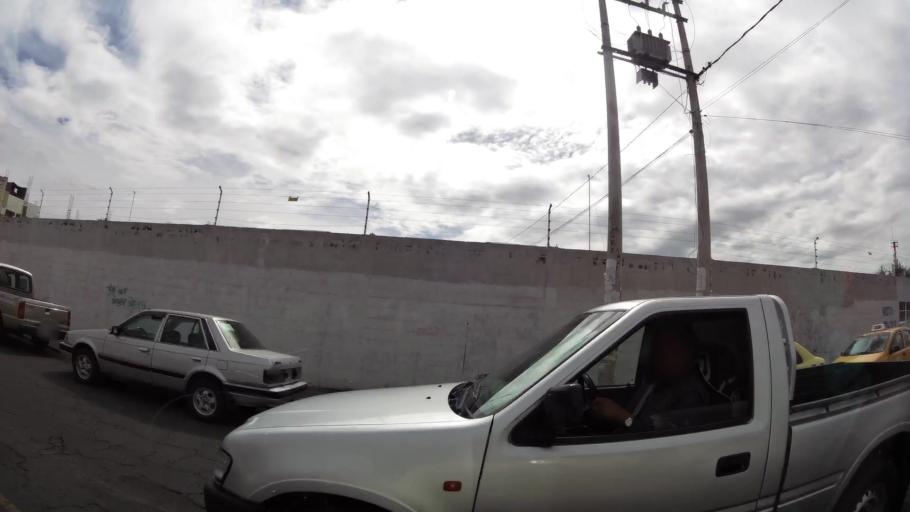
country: EC
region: Cotopaxi
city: Latacunga
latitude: -0.9211
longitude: -78.6218
